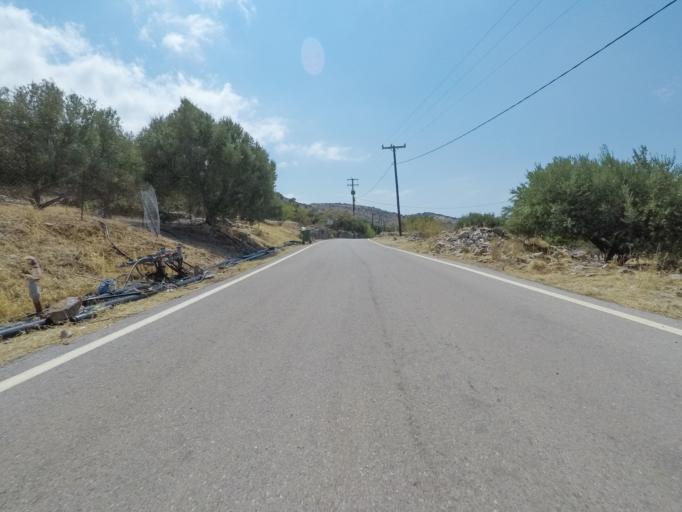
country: GR
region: Crete
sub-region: Nomos Lasithiou
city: Elounda
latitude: 35.3176
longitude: 25.6851
